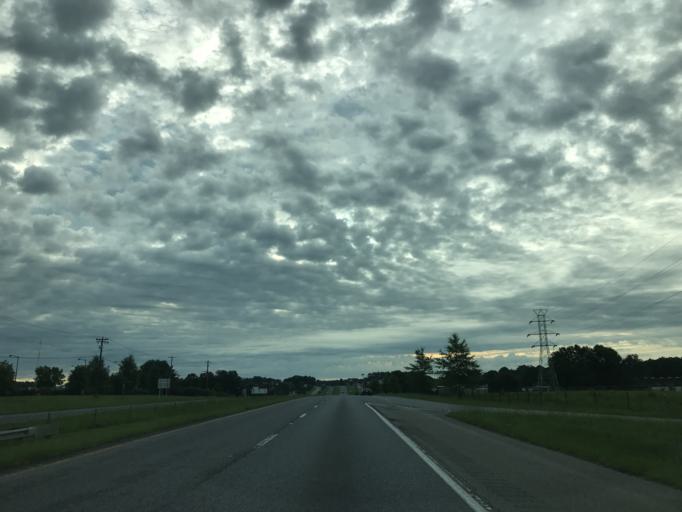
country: US
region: South Carolina
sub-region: Spartanburg County
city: Arcadia
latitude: 34.9700
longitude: -81.9990
